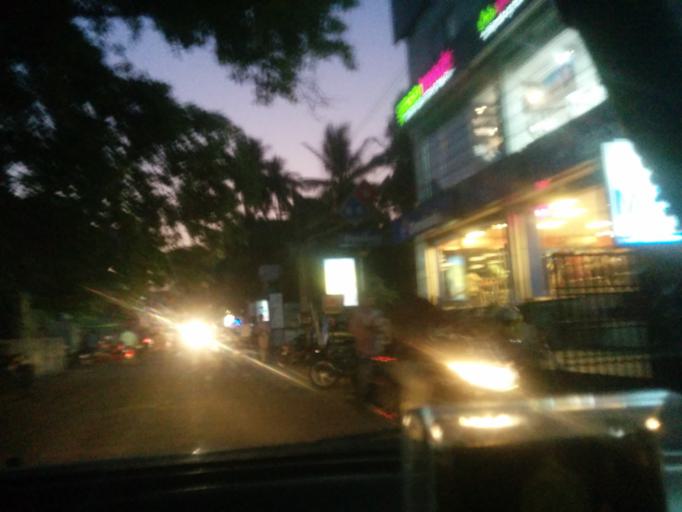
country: IN
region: Andhra Pradesh
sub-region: East Godavari
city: Rajahmundry
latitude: 17.0080
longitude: 81.7830
